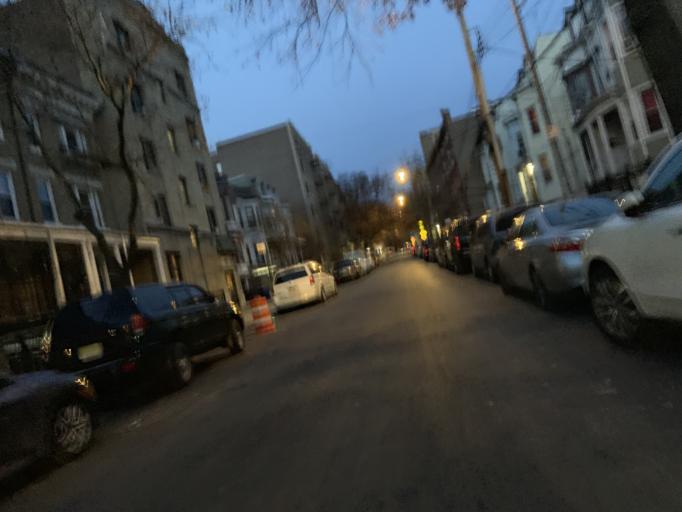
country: US
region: New York
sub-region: Bronx
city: The Bronx
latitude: 40.8657
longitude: -73.8922
